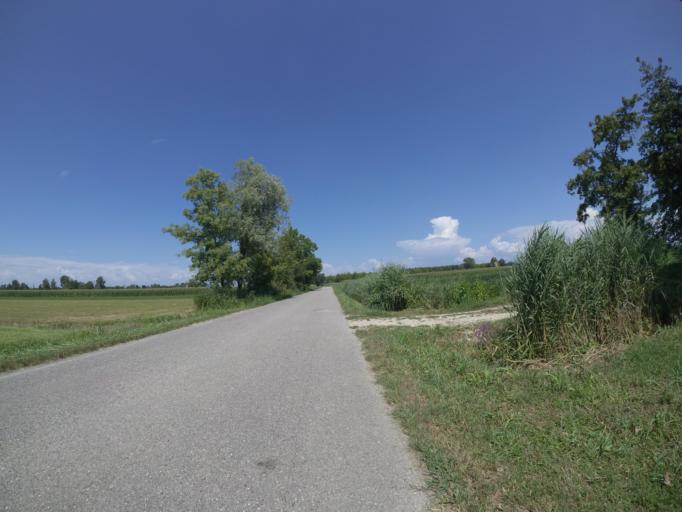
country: IT
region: Friuli Venezia Giulia
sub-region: Provincia di Udine
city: Talmassons
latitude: 45.9007
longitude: 13.1171
